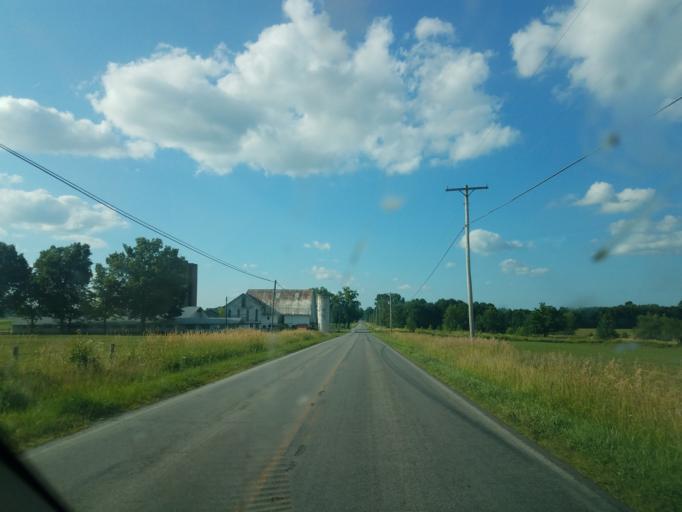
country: US
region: Ohio
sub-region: Wayne County
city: Apple Creek
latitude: 40.7490
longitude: -81.8959
